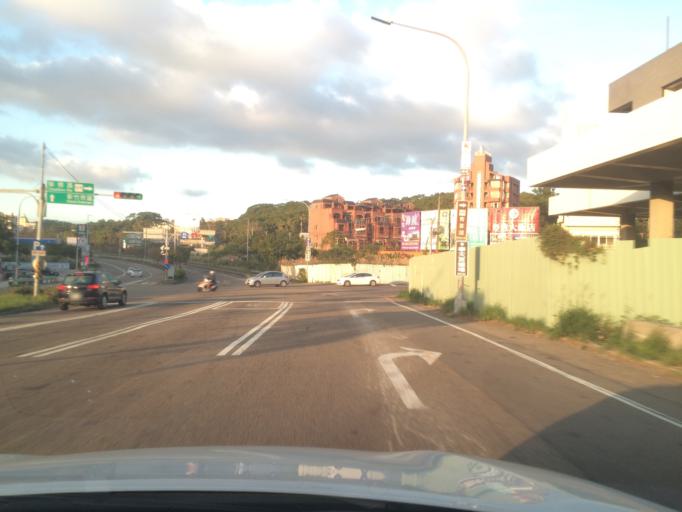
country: TW
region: Taiwan
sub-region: Hsinchu
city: Hsinchu
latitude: 24.7593
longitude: 120.9583
